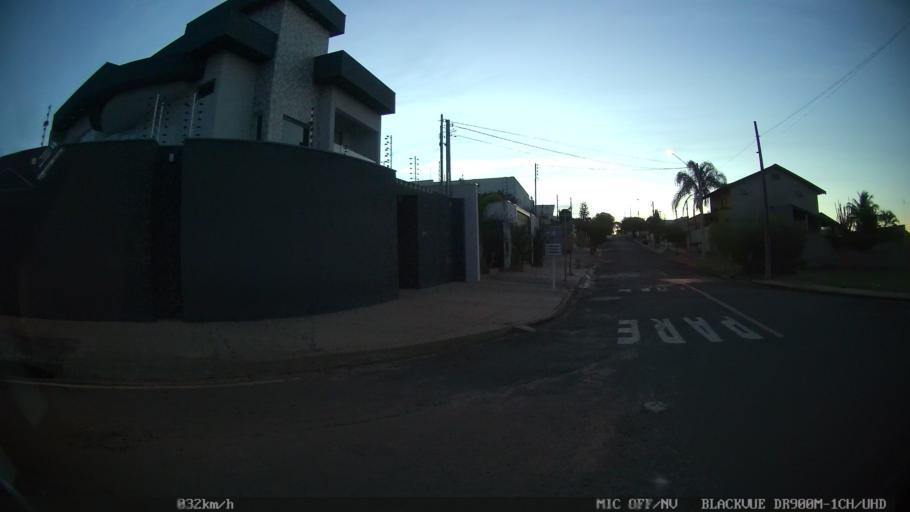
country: BR
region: Sao Paulo
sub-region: Catanduva
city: Catanduva
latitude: -21.1446
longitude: -48.9912
